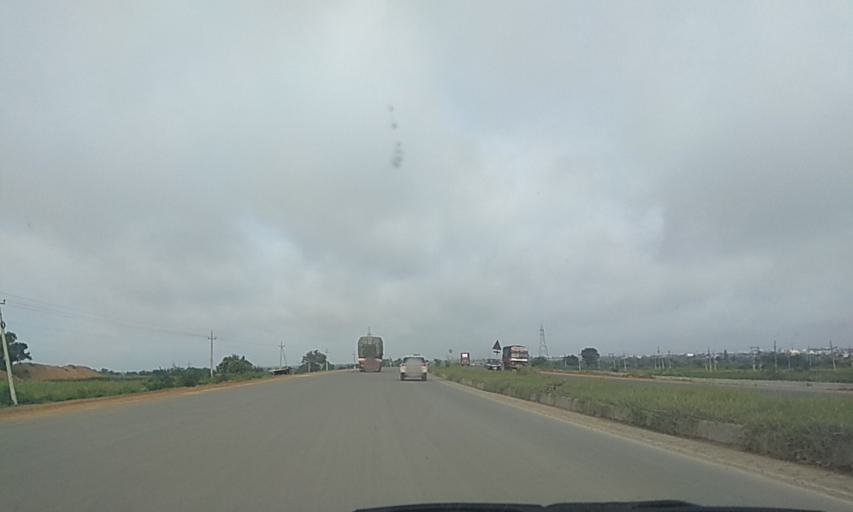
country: IN
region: Karnataka
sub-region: Haveri
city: Haveri
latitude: 14.7728
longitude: 75.4124
